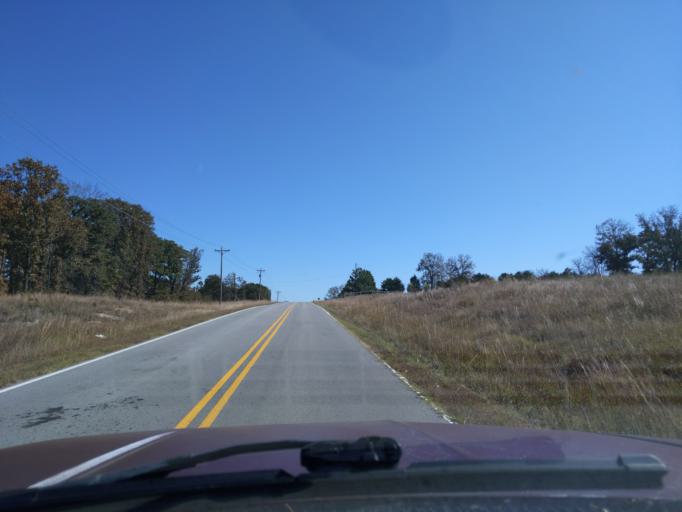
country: US
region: Oklahoma
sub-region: Creek County
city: Bristow
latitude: 35.7119
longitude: -96.3923
